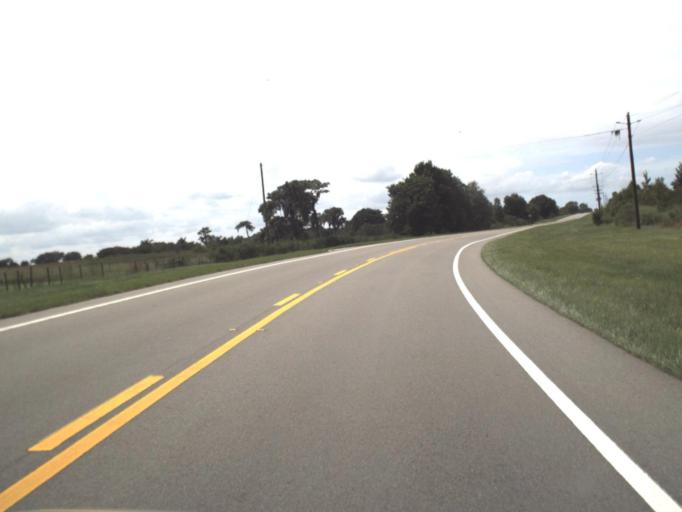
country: US
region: Florida
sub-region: Hillsborough County
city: Wimauma
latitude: 27.5873
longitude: -82.2341
